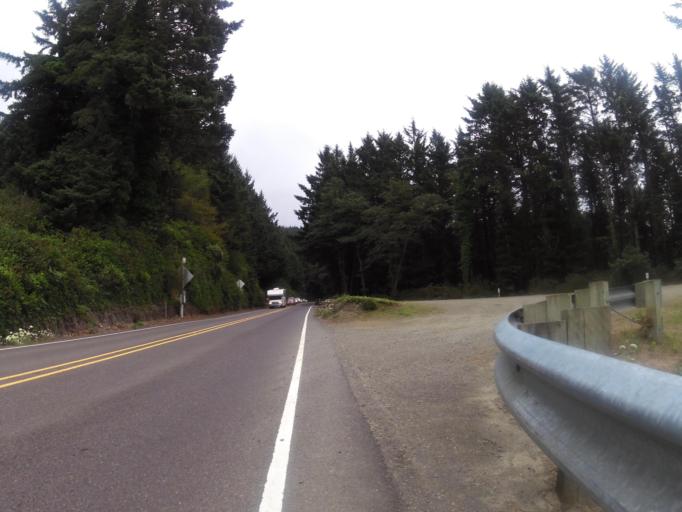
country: US
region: Oregon
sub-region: Lane County
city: Florence
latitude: 44.1207
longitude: -124.1249
